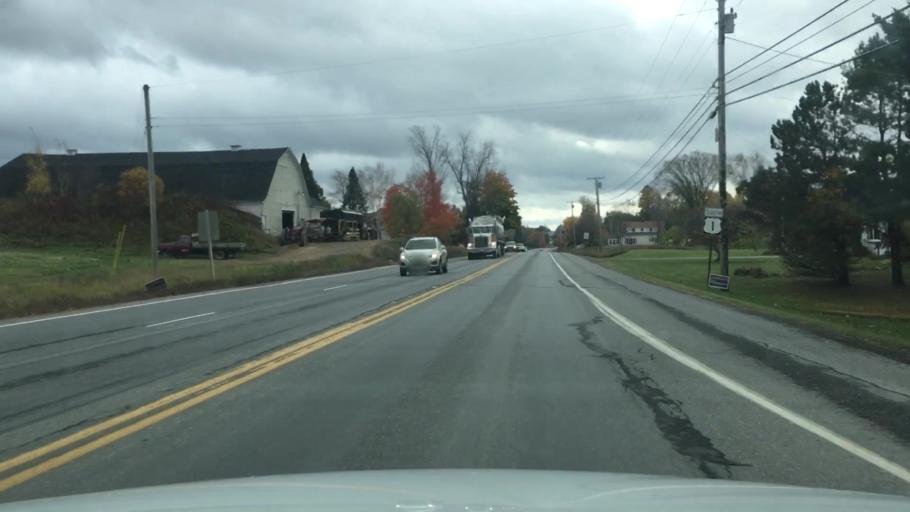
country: US
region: Maine
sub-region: Aroostook County
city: Houlton
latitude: 46.2168
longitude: -67.8410
